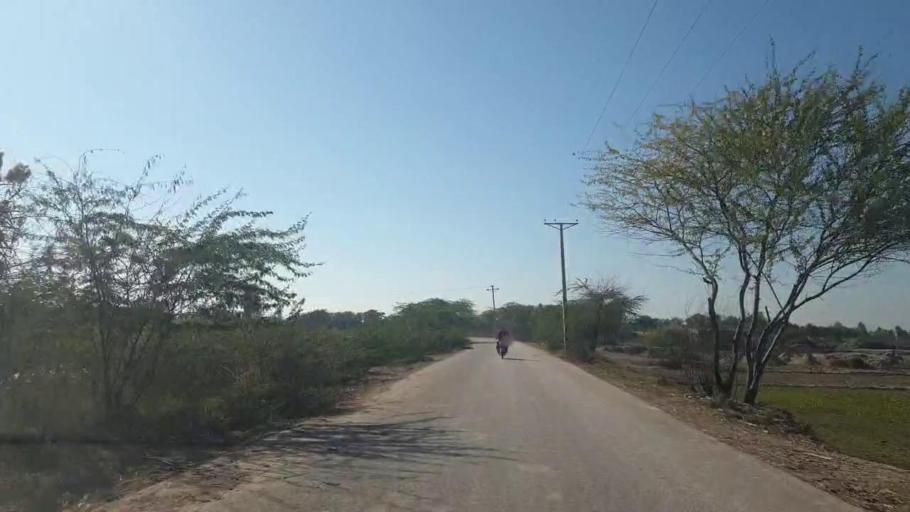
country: PK
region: Sindh
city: Kot Diji
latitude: 27.2982
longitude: 68.6416
